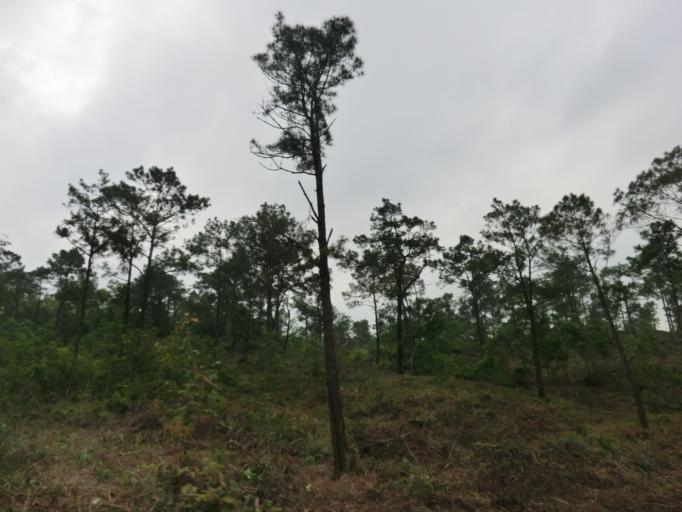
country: VN
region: Quang Binh
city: Ba Don
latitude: 17.6677
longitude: 106.4274
